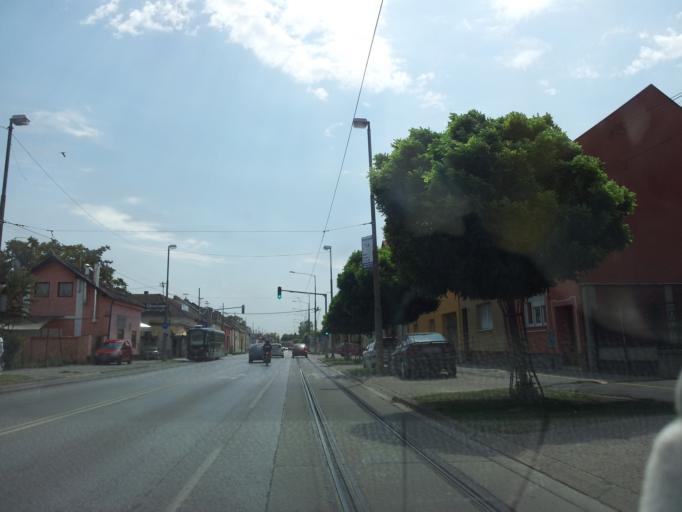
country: HR
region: Osjecko-Baranjska
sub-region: Grad Osijek
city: Osijek
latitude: 45.5506
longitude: 18.6777
